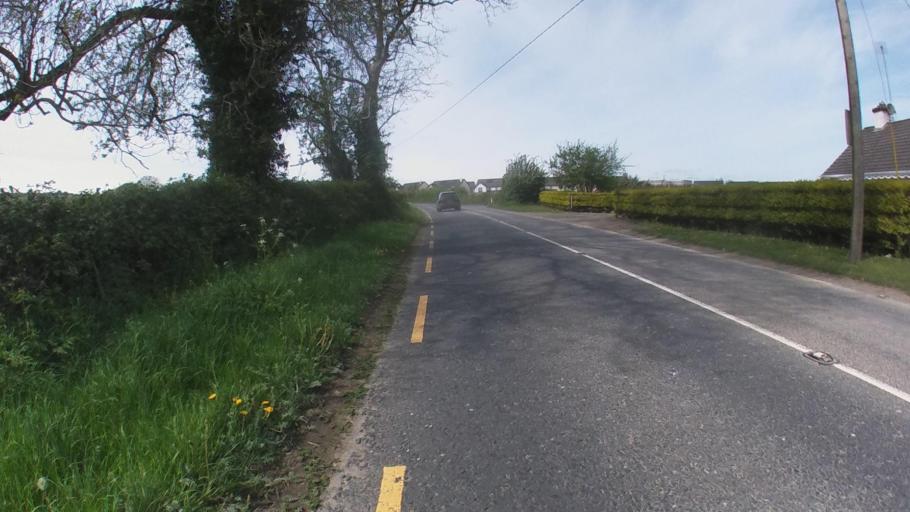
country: IE
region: Leinster
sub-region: County Carlow
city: Carlow
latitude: 52.8474
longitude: -6.9881
